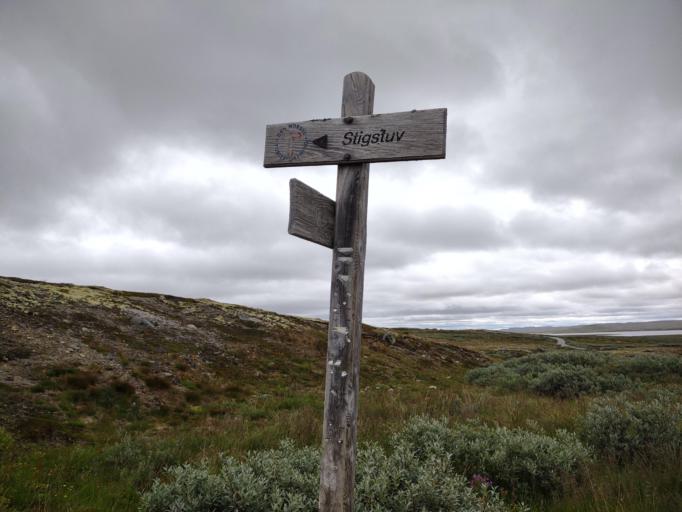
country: NO
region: Hordaland
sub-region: Eidfjord
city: Eidfjord
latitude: 60.2849
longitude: 7.5755
